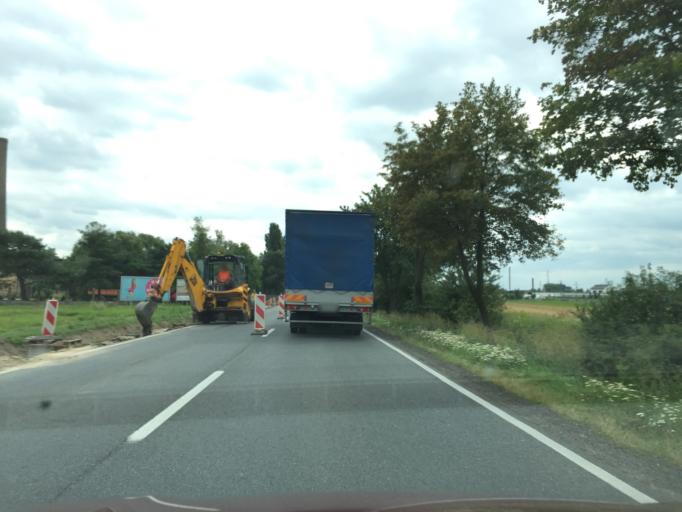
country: PL
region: Greater Poland Voivodeship
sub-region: Kalisz
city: Kalisz
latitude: 51.7941
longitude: 18.0912
